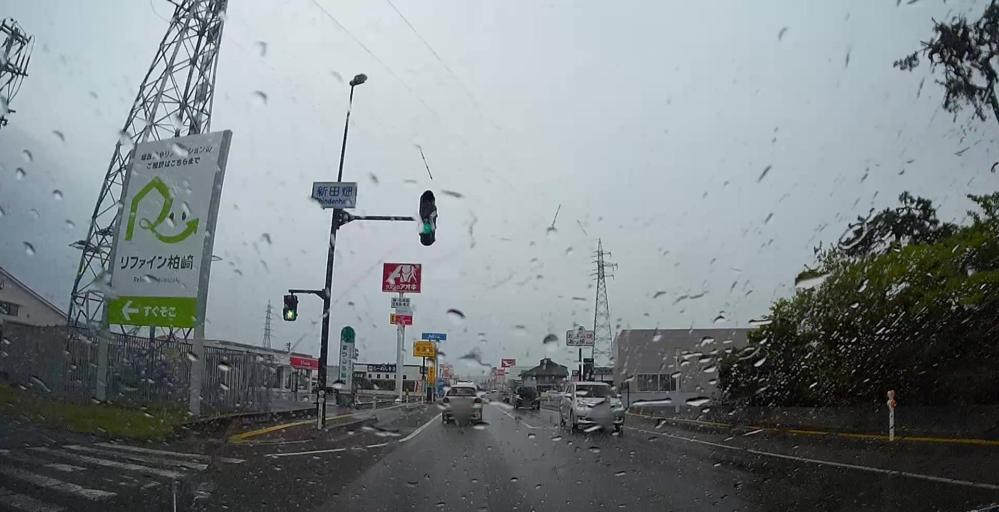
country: JP
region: Niigata
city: Kashiwazaki
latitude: 37.3750
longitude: 138.5794
